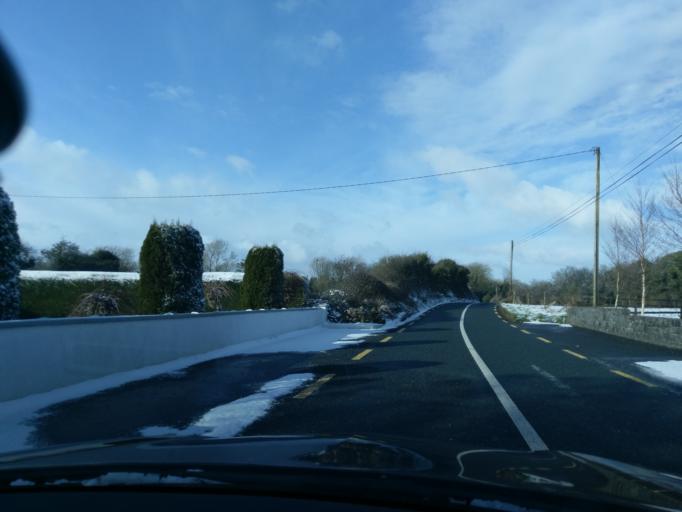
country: IE
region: Connaught
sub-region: County Galway
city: Athenry
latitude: 53.1945
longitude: -8.7623
